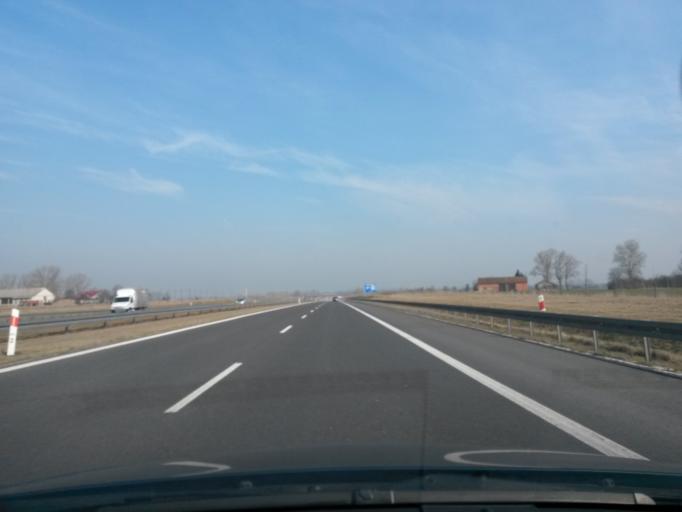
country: PL
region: Lodz Voivodeship
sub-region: Powiat kutnowski
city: Krzyzanow
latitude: 52.1603
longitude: 19.4833
